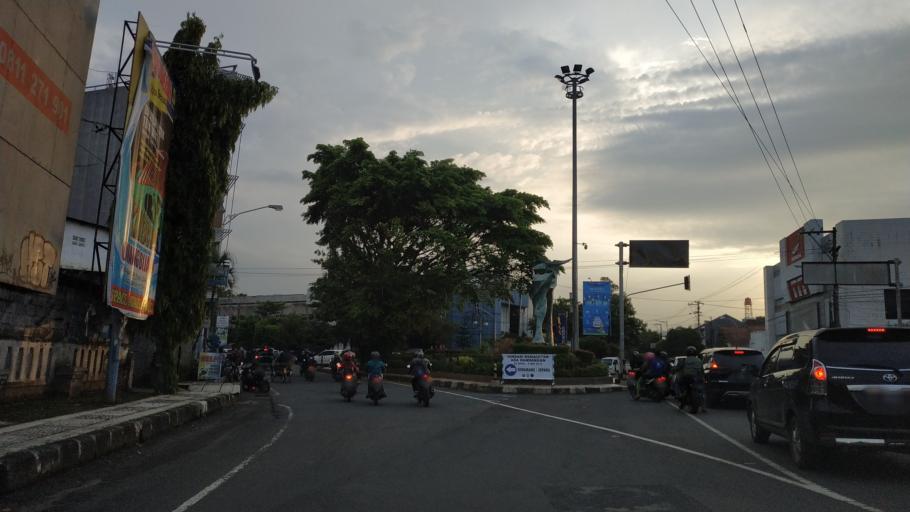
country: ID
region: Central Java
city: Kudus
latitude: -6.8037
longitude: 110.8577
